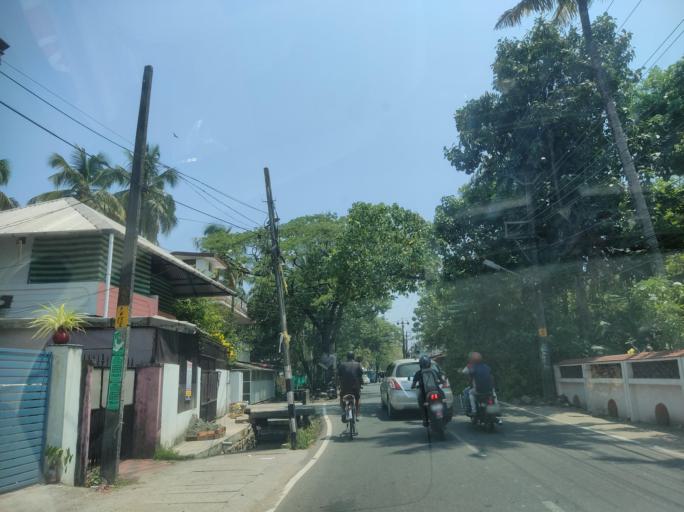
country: IN
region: Kerala
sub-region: Ernakulam
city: Cochin
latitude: 9.9061
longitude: 76.2808
